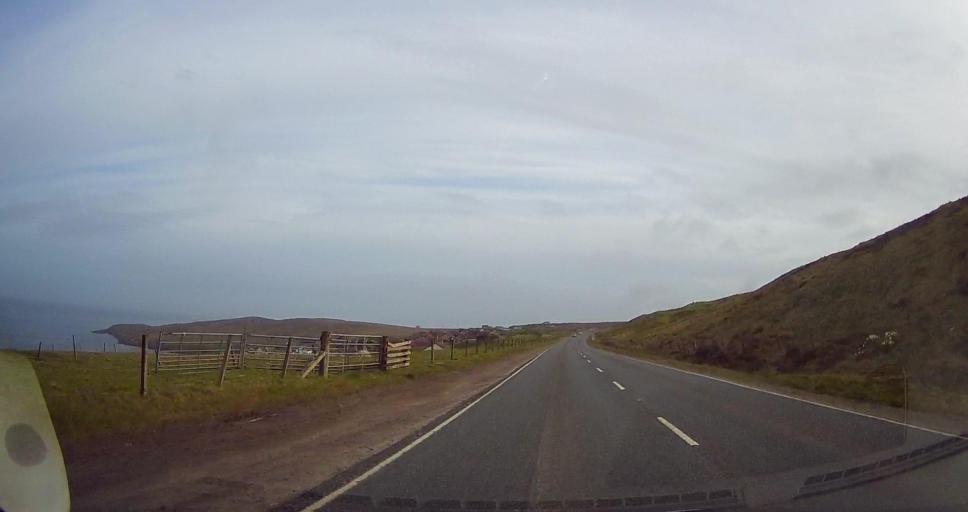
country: GB
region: Scotland
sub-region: Shetland Islands
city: Lerwick
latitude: 60.1328
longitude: -1.2142
